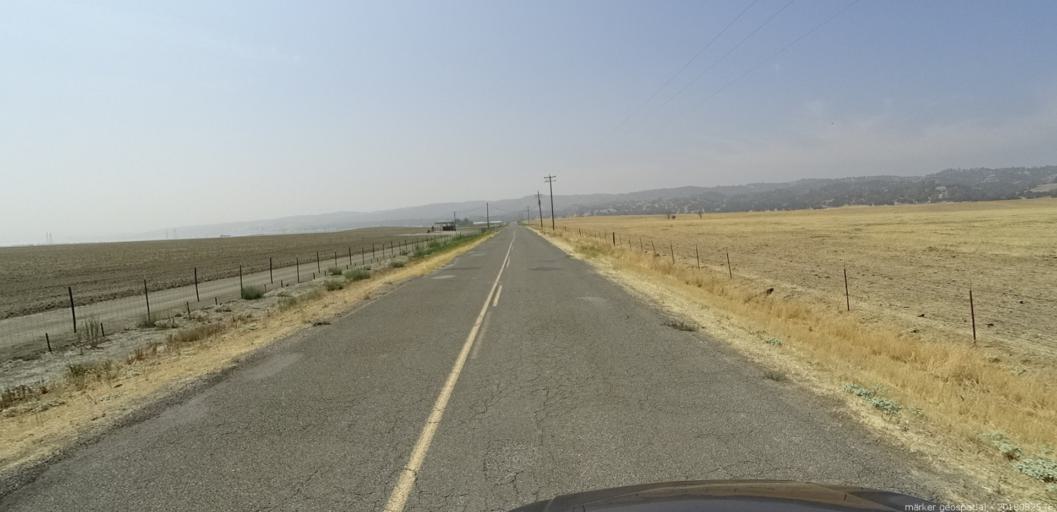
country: US
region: California
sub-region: San Luis Obispo County
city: Shandon
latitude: 35.8439
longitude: -120.3801
